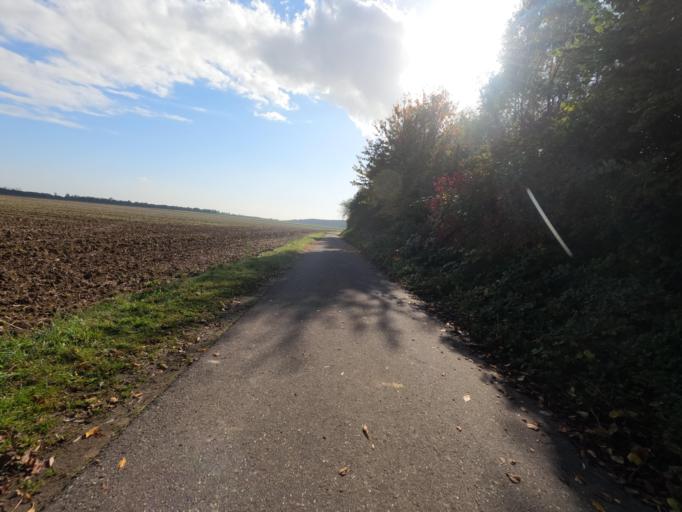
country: DE
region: North Rhine-Westphalia
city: Neu-Pattern
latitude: 50.8661
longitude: 6.2987
